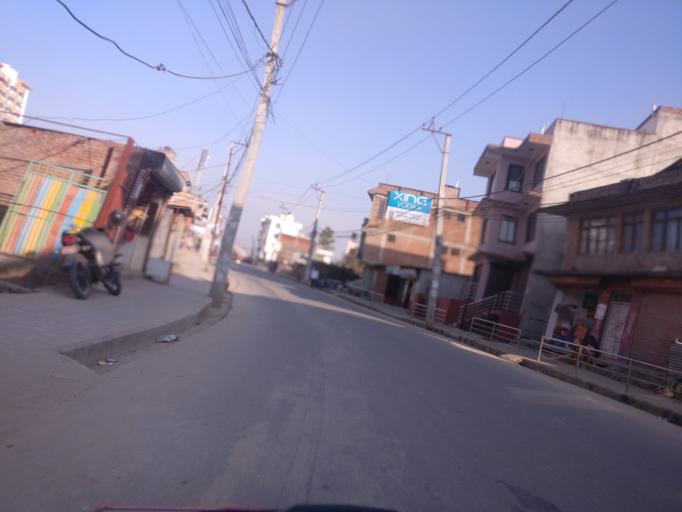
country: NP
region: Central Region
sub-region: Bagmati Zone
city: Patan
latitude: 27.6716
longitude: 85.3371
